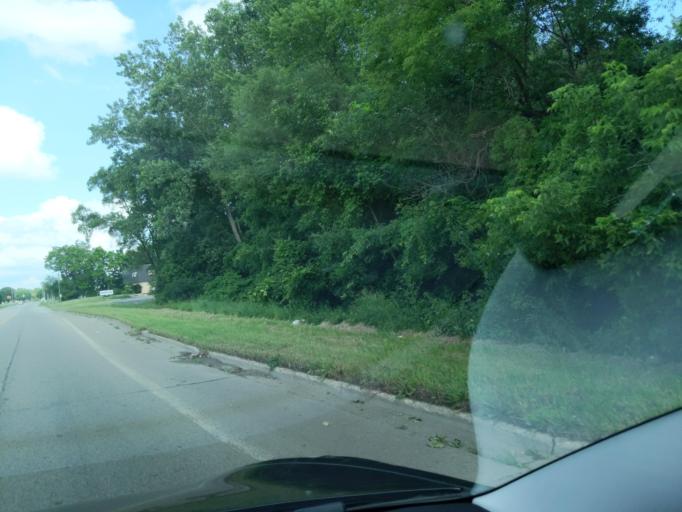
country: US
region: Michigan
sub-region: Jackson County
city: Jackson
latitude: 42.2331
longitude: -84.3879
